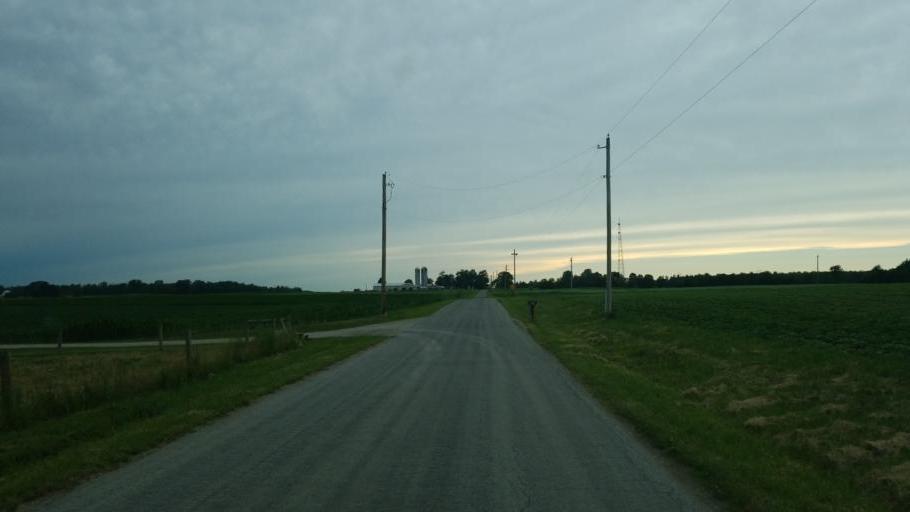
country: US
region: Ohio
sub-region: Huron County
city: Greenwich
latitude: 40.9387
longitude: -82.4684
